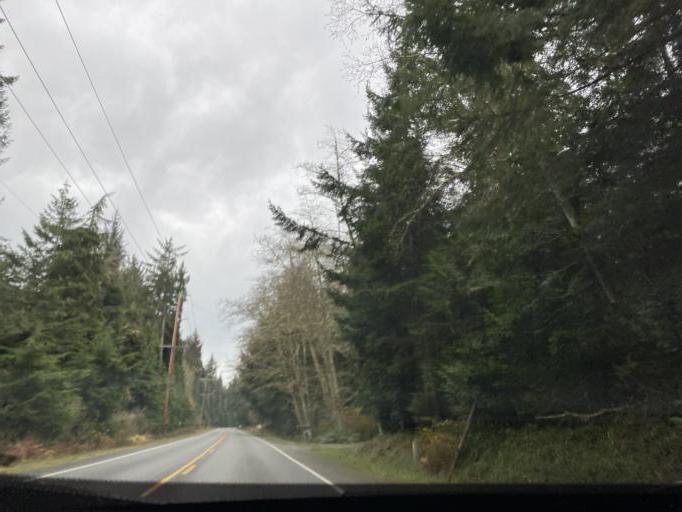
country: US
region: Washington
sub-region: Island County
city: Freeland
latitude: 48.0485
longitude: -122.5892
